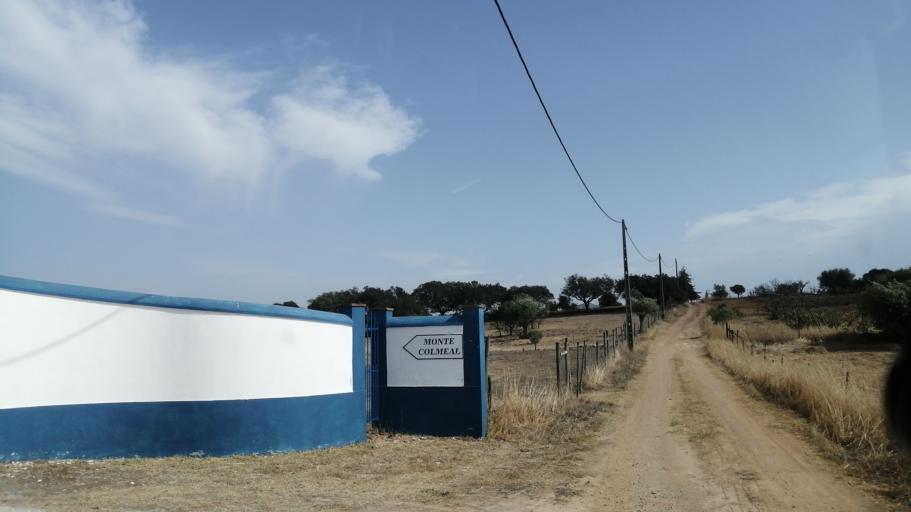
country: PT
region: Evora
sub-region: Mourao
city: Mourao
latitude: 38.3927
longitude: -7.3183
